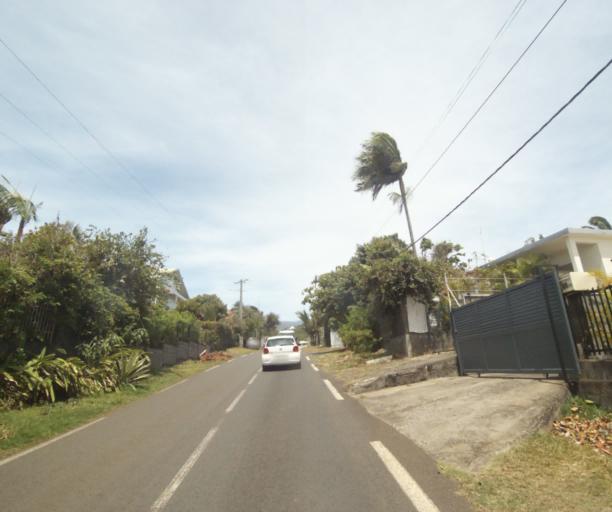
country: RE
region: Reunion
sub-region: Reunion
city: Saint-Paul
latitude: -21.0478
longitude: 55.2730
